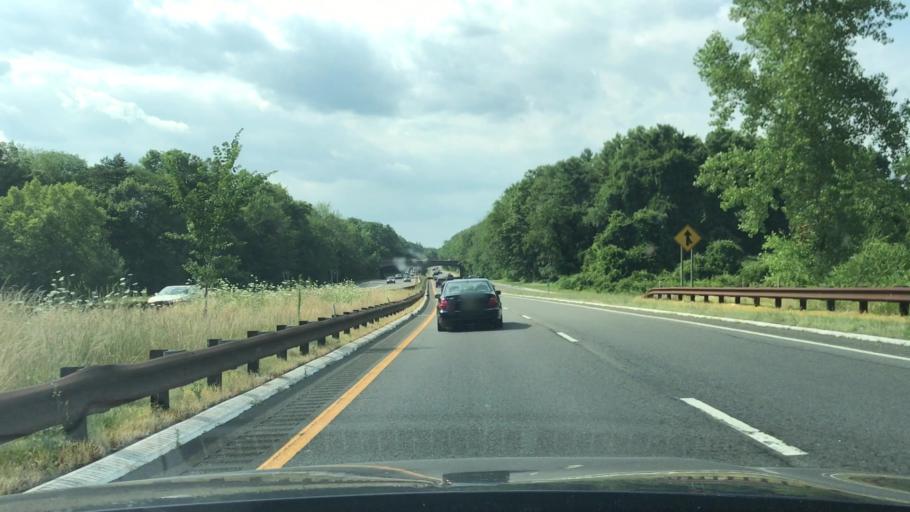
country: US
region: New York
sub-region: Rockland County
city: Bardonia
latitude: 41.1038
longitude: -73.9941
